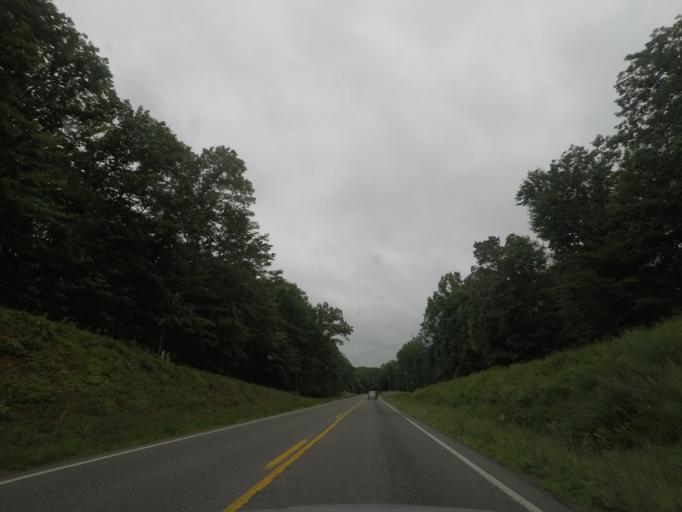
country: US
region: Virginia
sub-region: Fluvanna County
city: Palmyra
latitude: 37.8190
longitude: -78.2637
